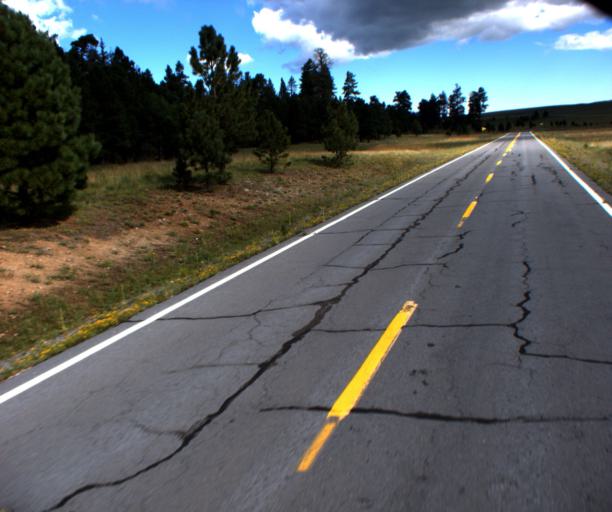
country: US
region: Arizona
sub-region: Apache County
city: Eagar
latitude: 33.9218
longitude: -109.4121
